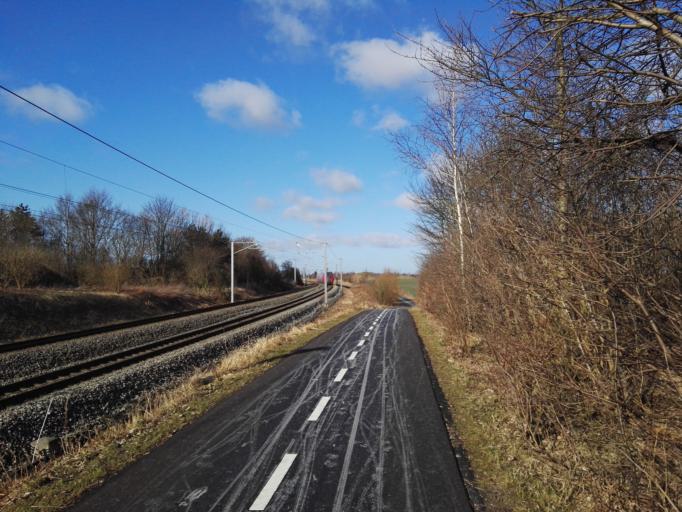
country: DK
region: Capital Region
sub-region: Egedal Kommune
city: Stenlose
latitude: 55.7822
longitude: 12.1848
